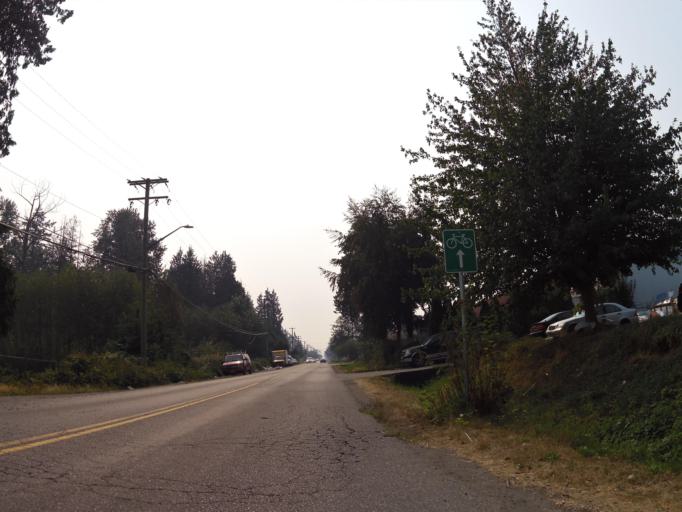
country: CA
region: British Columbia
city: Delta
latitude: 49.1555
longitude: -122.8791
